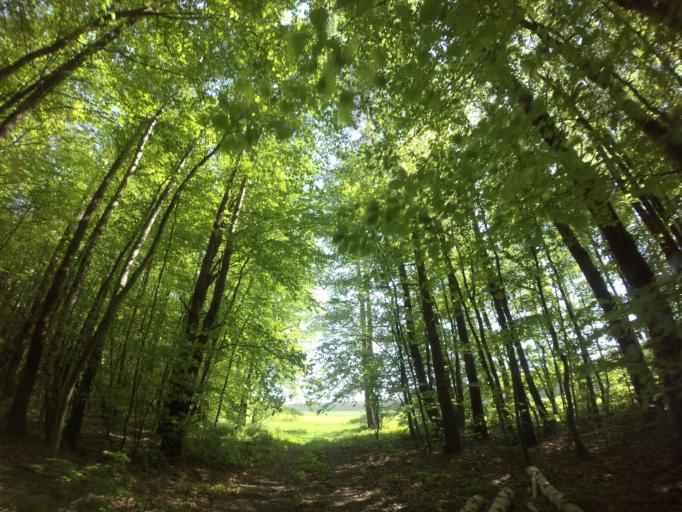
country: PL
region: West Pomeranian Voivodeship
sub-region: Powiat choszczenski
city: Pelczyce
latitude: 52.9471
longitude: 15.3376
